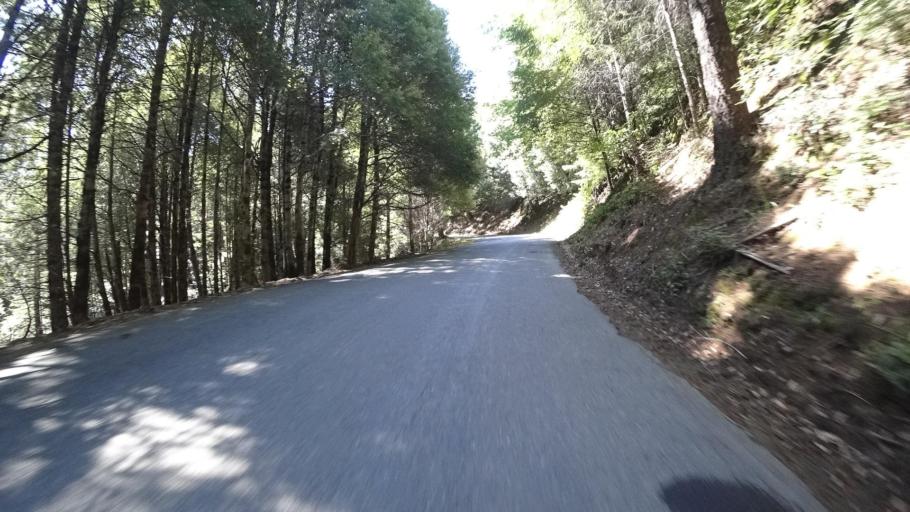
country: US
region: California
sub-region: Humboldt County
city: Redway
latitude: 40.1318
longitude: -123.9781
